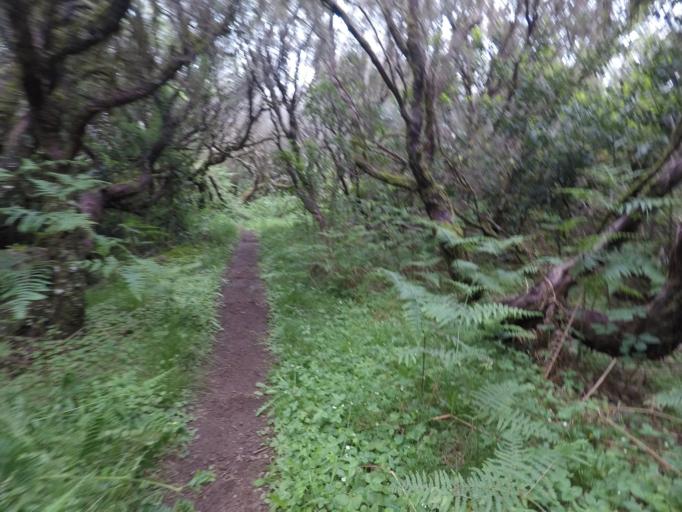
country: PT
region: Madeira
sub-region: Sao Vicente
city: Sao Vicente
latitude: 32.7715
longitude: -17.0620
